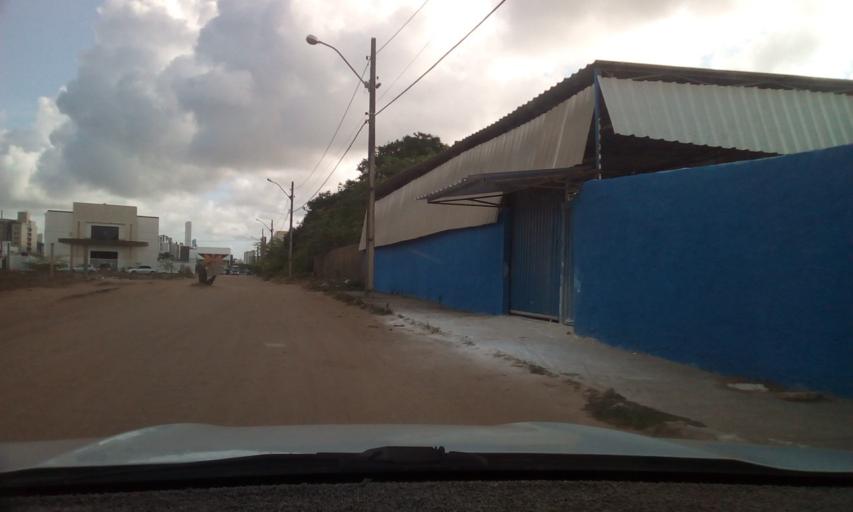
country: BR
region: Paraiba
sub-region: Joao Pessoa
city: Joao Pessoa
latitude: -7.0786
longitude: -34.8463
